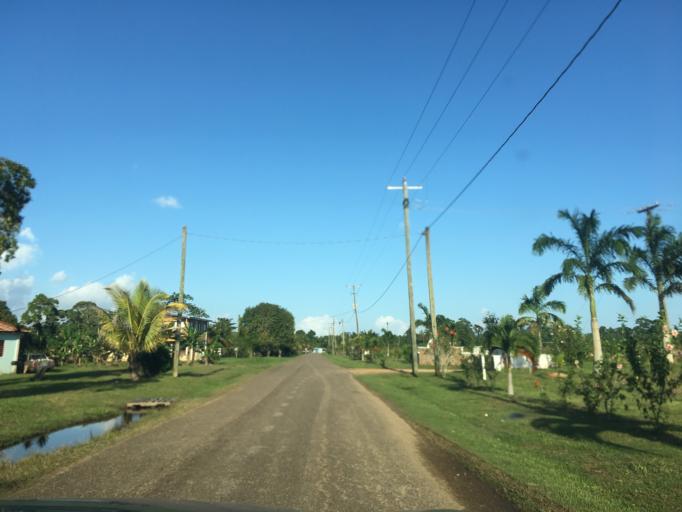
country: BZ
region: Stann Creek
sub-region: Dangriga
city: Dangriga
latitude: 16.8194
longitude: -88.3303
